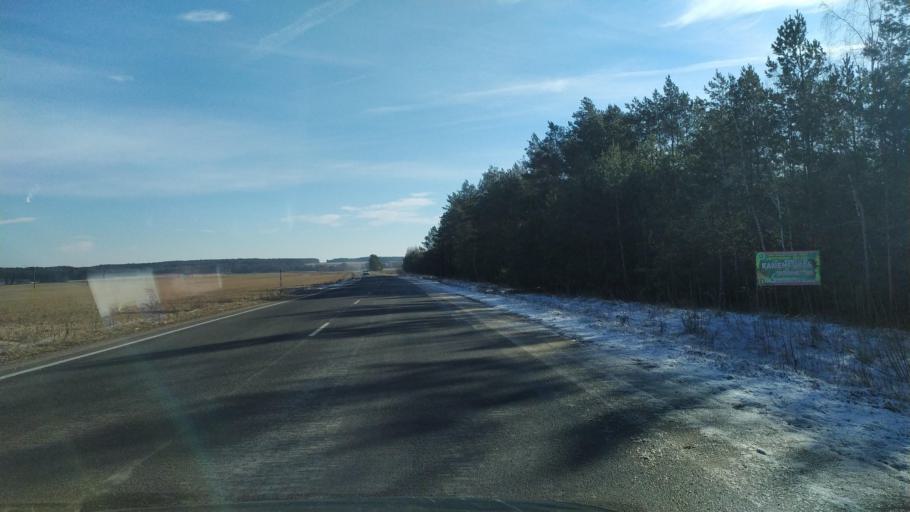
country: BY
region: Brest
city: Kamyanyets
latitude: 52.4016
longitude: 23.8723
